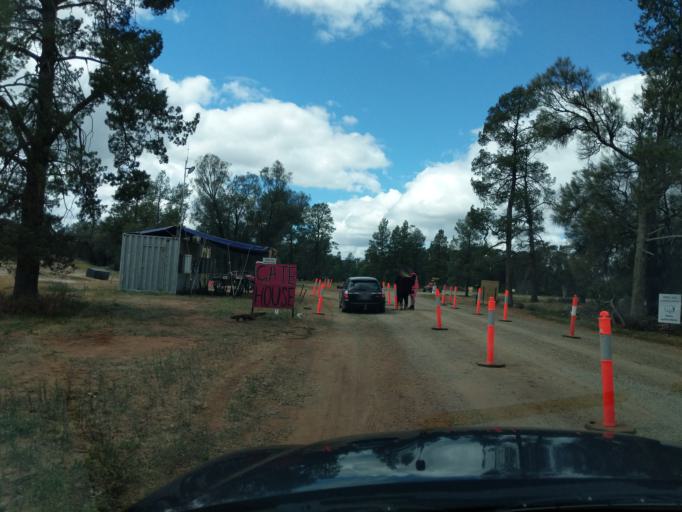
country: AU
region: New South Wales
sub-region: Coolamon
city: Coolamon
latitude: -34.8551
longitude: 146.9167
